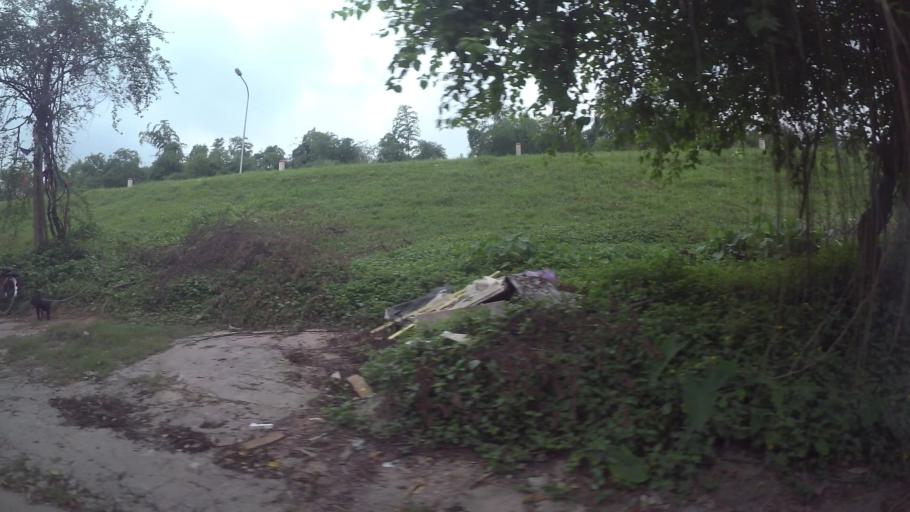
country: VN
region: Ha Noi
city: Trau Quy
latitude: 21.0500
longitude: 105.9252
